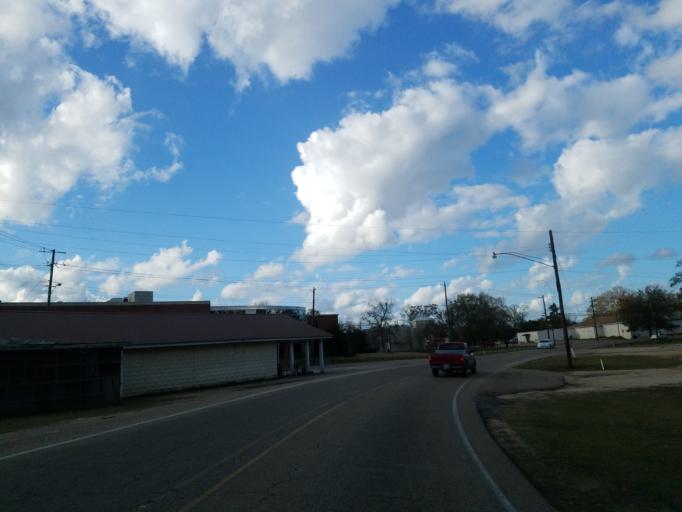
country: US
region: Mississippi
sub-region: Jones County
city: Ellisville
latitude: 31.5966
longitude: -89.1973
